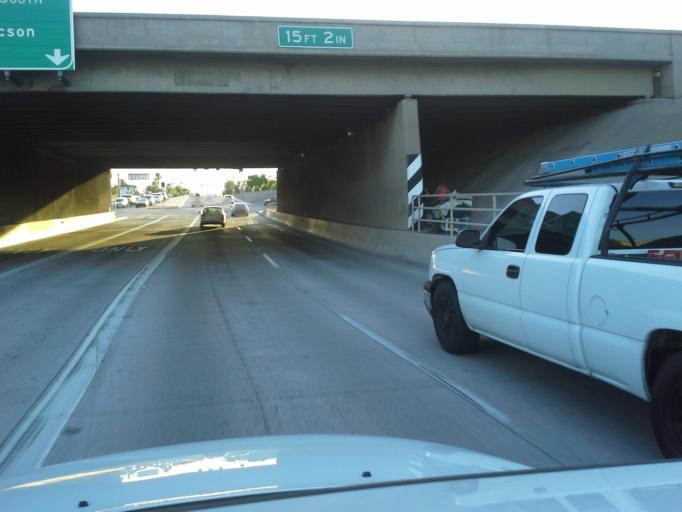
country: US
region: Arizona
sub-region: Maricopa County
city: Glendale
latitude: 33.6109
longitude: -112.1161
